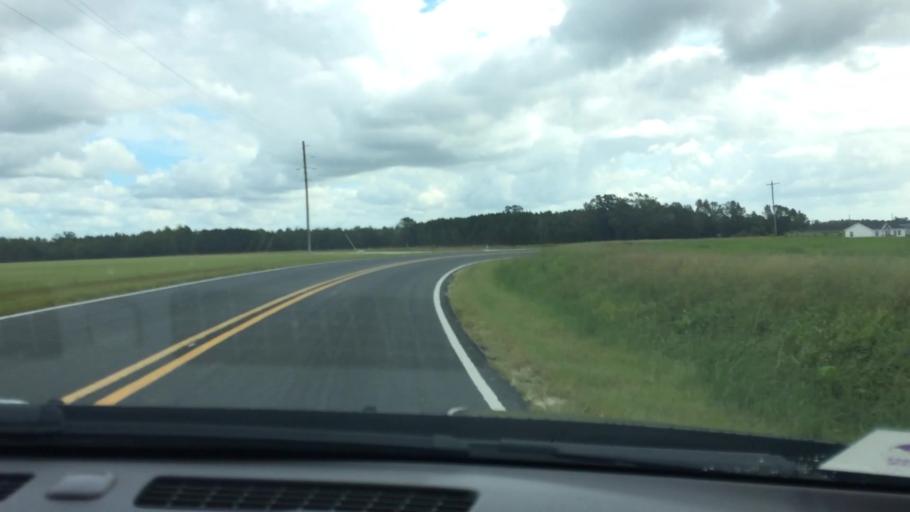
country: US
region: North Carolina
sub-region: Greene County
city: Maury
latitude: 35.5167
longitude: -77.5265
